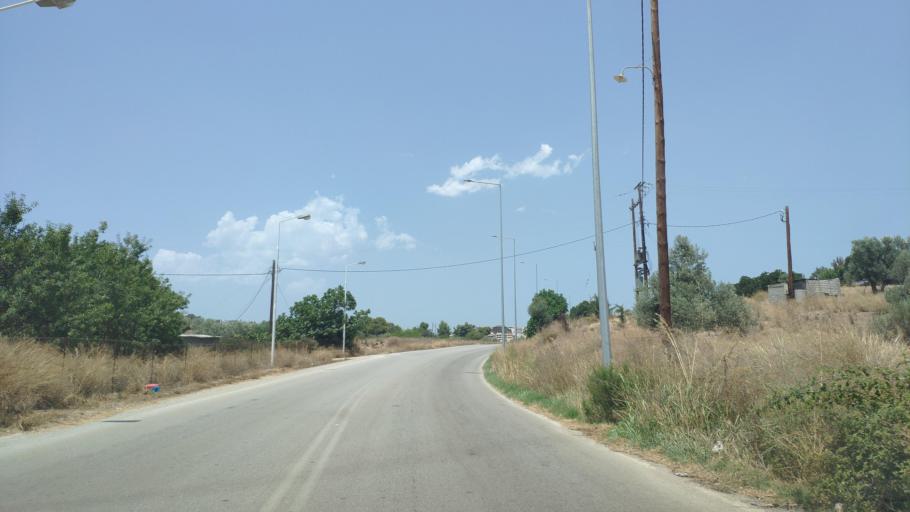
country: GR
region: Peloponnese
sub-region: Nomos Argolidos
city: Kranidi
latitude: 37.3665
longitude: 23.1621
